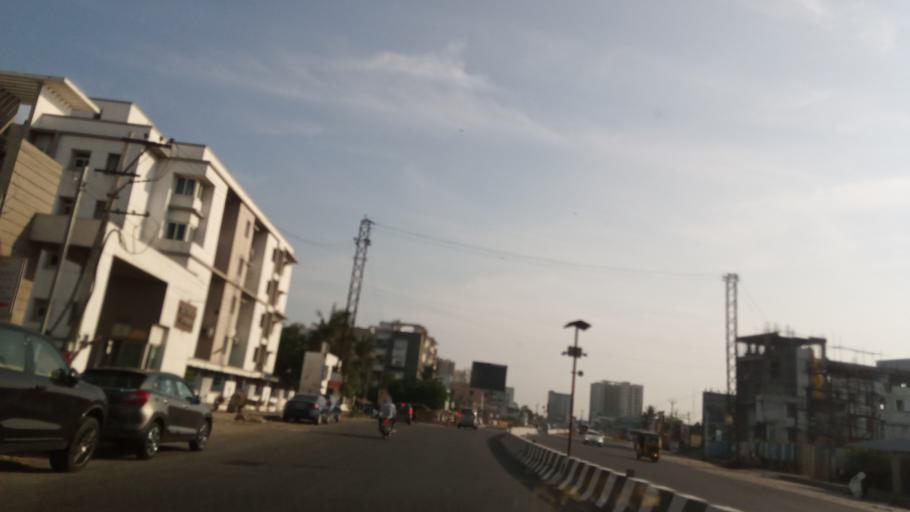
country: IN
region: Tamil Nadu
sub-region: Kancheepuram
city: Poonamalle
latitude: 13.0530
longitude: 80.1236
